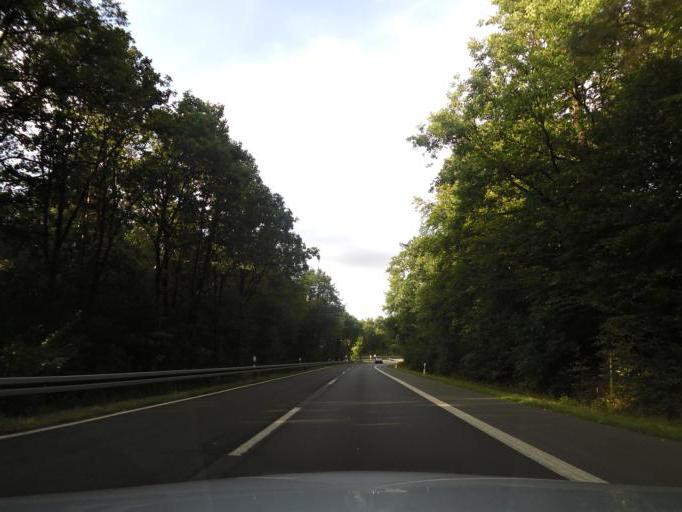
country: DE
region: Hesse
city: Niederrad
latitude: 50.0580
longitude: 8.6509
